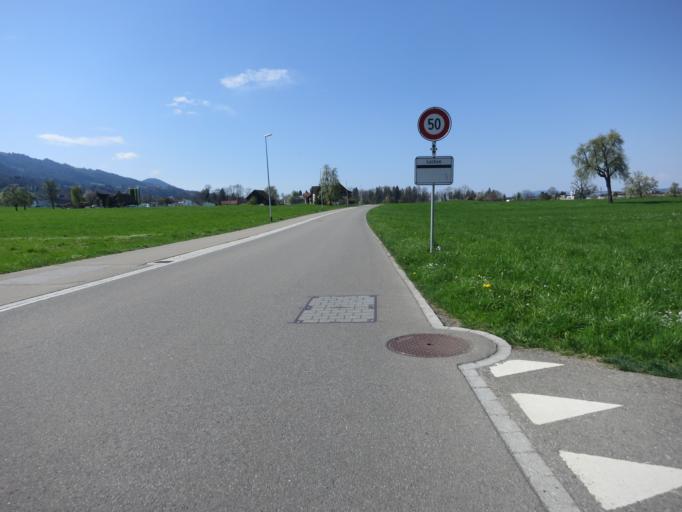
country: CH
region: Schwyz
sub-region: Bezirk March
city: Lachen
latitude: 47.1814
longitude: 8.8653
